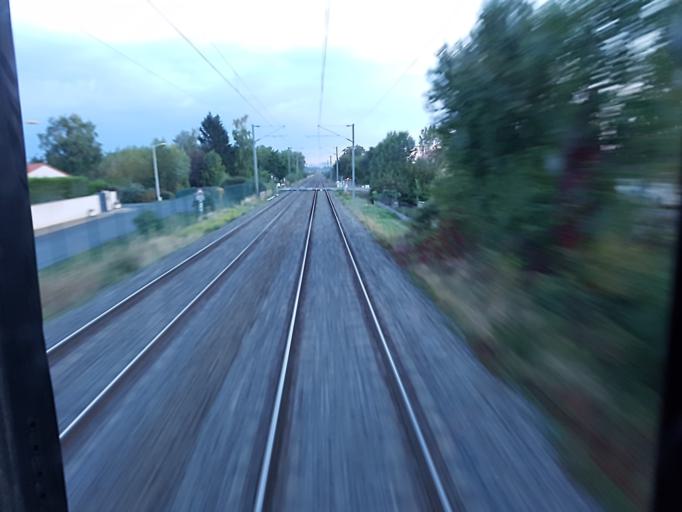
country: FR
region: Auvergne
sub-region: Departement du Puy-de-Dome
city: Menetrol
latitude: 45.8720
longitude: 3.1276
